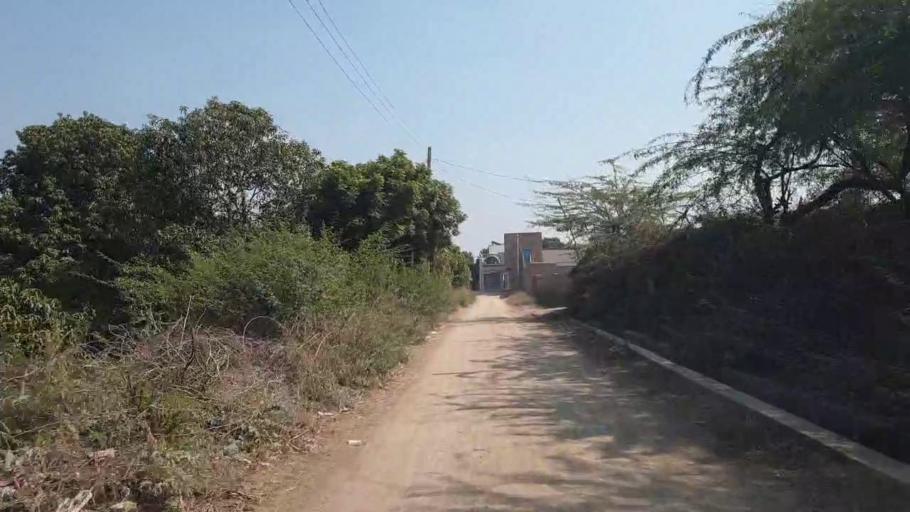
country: PK
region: Sindh
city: Chambar
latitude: 25.4138
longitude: 68.8987
